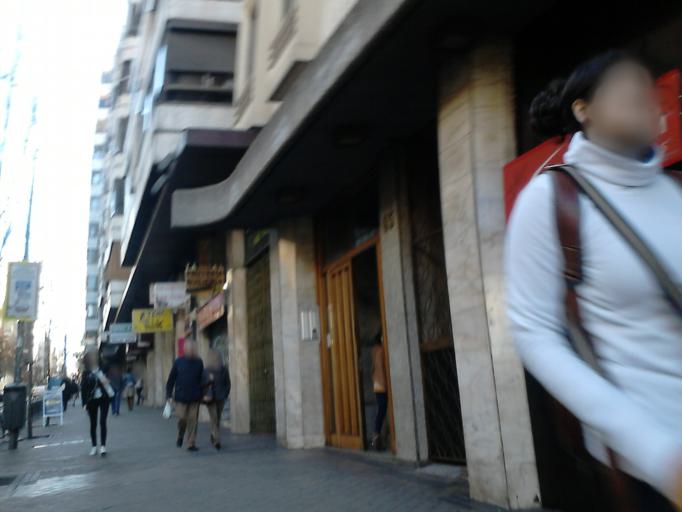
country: ES
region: Madrid
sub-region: Provincia de Madrid
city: Moncloa-Aravaca
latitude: 40.4355
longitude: -3.7181
